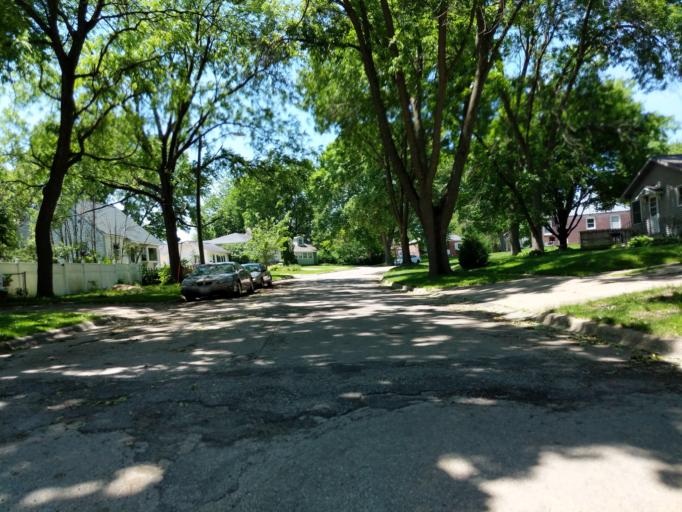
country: US
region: Iowa
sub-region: Linn County
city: Cedar Rapids
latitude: 42.0178
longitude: -91.6355
